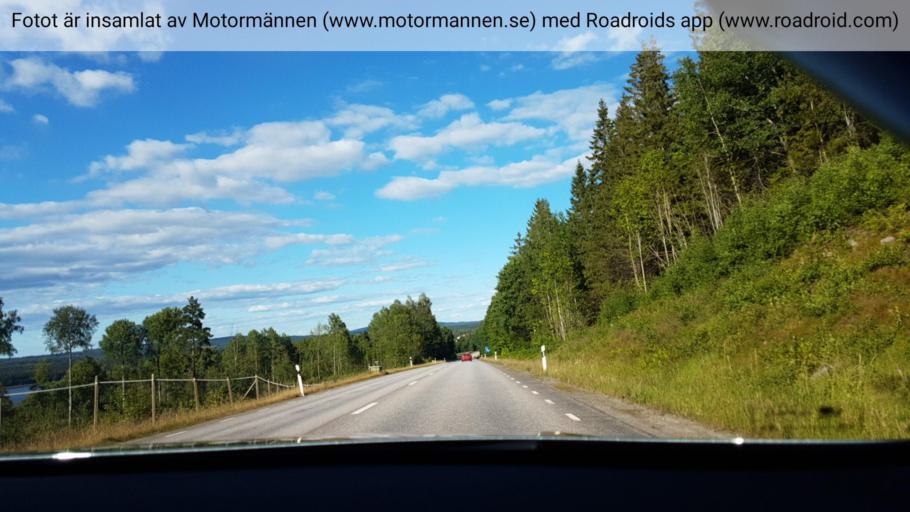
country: SE
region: Vaestra Goetaland
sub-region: Tibro Kommun
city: Tibro
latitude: 58.4601
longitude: 14.2814
